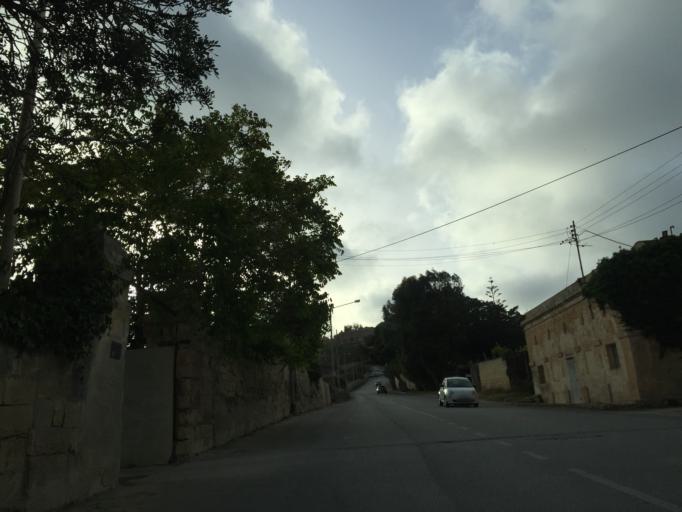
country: MT
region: L-Imdina
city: Imdina
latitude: 35.8816
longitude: 14.4072
